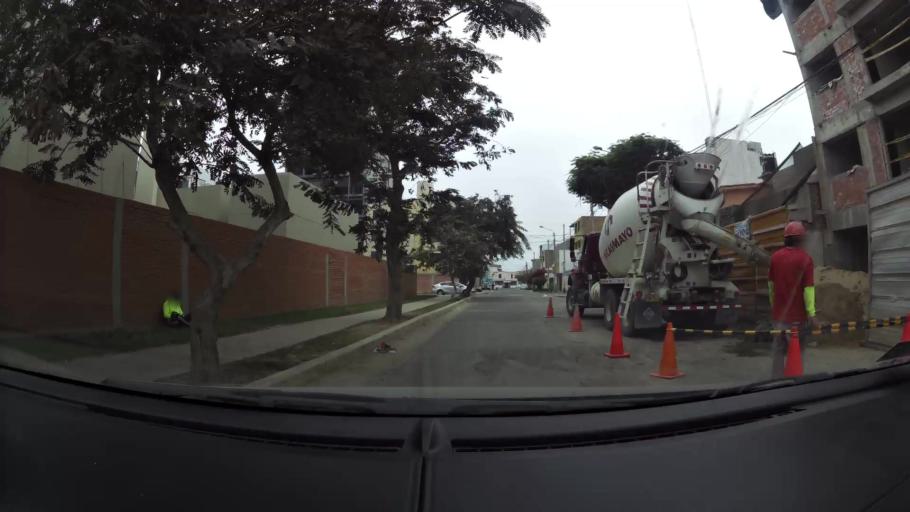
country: PE
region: La Libertad
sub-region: Provincia de Trujillo
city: Buenos Aires
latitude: -8.1328
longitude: -79.0398
